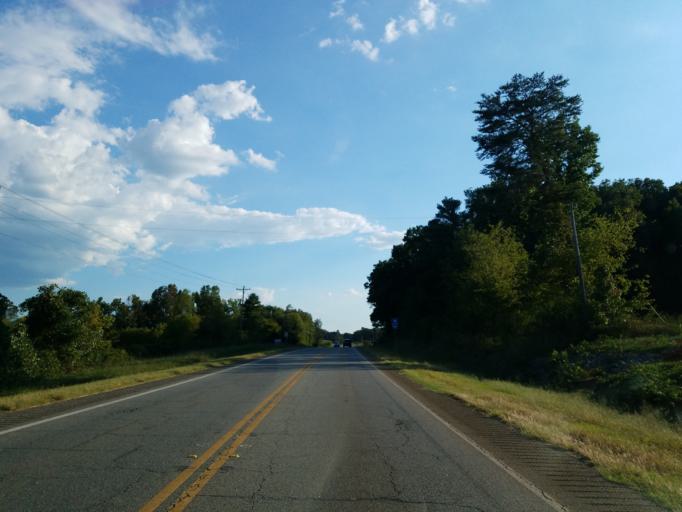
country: US
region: Georgia
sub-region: Murray County
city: Chatsworth
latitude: 34.8797
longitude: -84.7505
